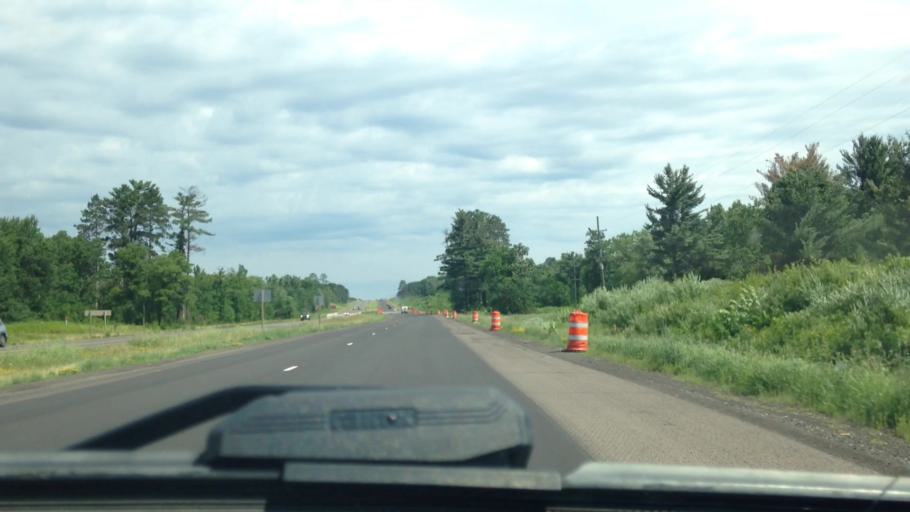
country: US
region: Wisconsin
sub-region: Washburn County
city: Spooner
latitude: 46.1393
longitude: -91.8159
